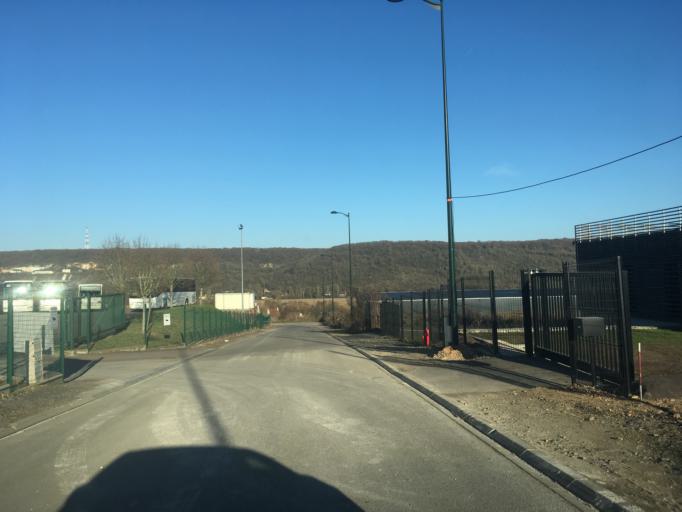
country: FR
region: Haute-Normandie
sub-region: Departement de l'Eure
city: Vernon
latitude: 49.0781
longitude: 1.5010
